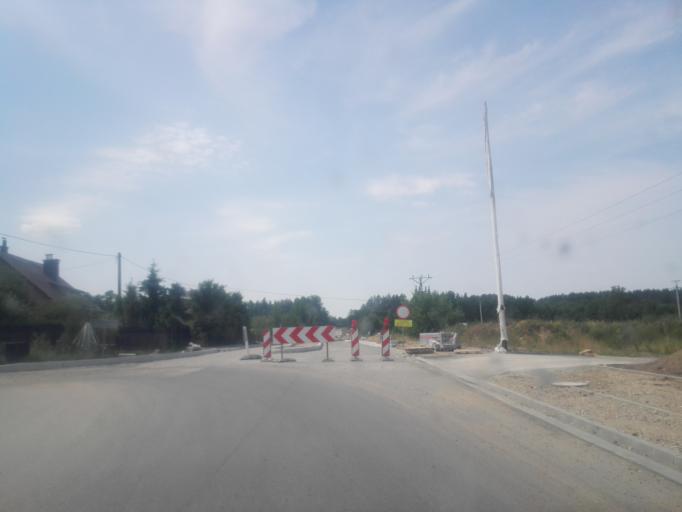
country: PL
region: Podlasie
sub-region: Powiat sejnenski
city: Krasnopol
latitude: 54.0916
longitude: 23.1450
